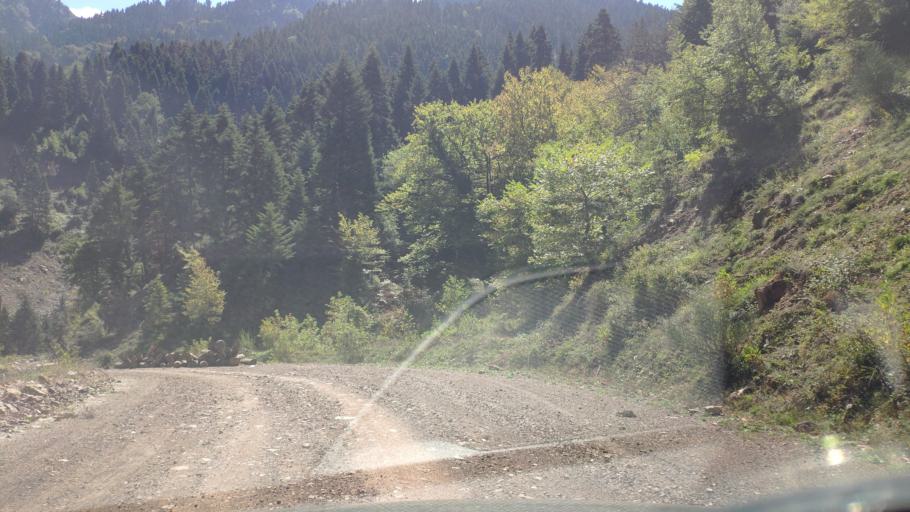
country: GR
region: Central Greece
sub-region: Nomos Evrytanias
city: Kerasochori
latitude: 39.1142
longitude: 21.6211
